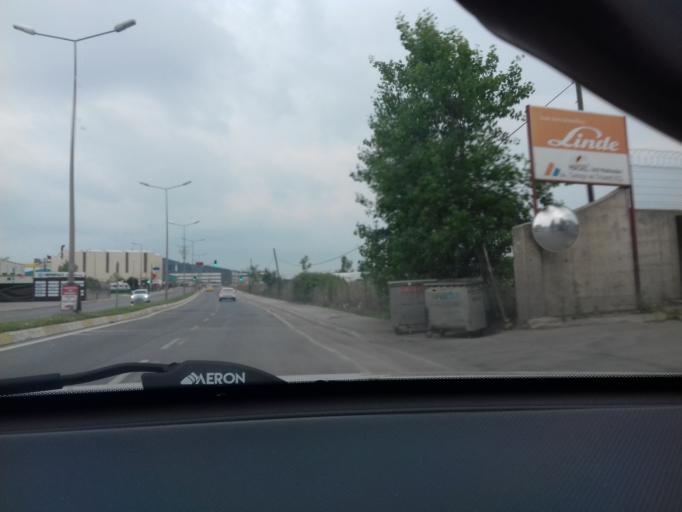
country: TR
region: Istanbul
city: Icmeler
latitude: 40.8904
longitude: 29.3536
